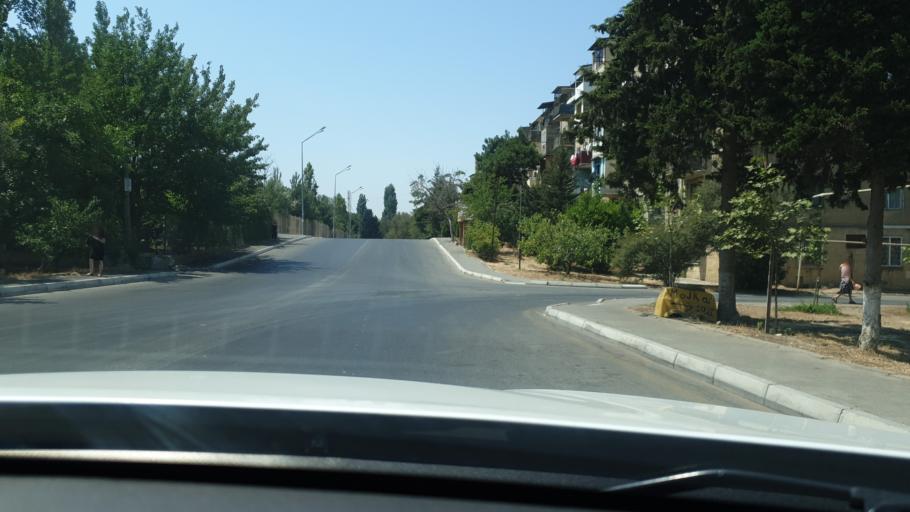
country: AZ
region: Baki
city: Bakixanov
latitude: 40.4163
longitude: 49.9464
